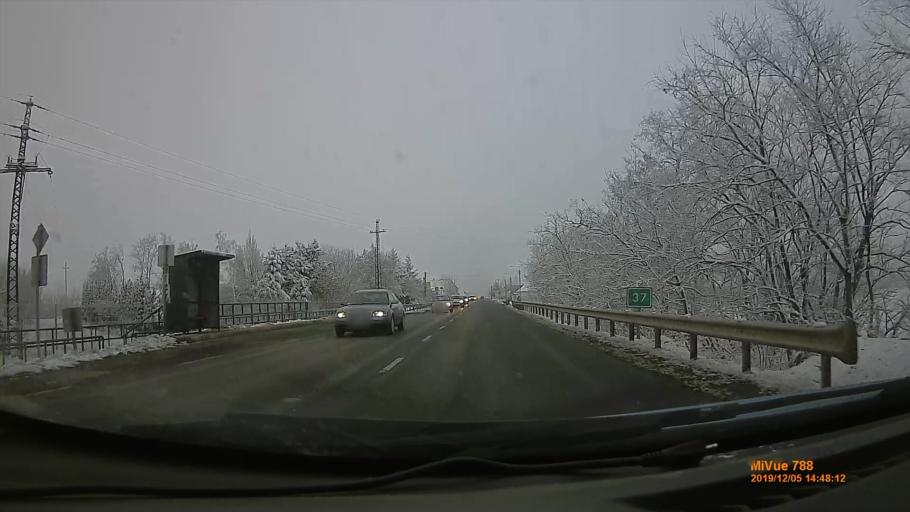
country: HU
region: Szabolcs-Szatmar-Bereg
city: Nyiregyhaza
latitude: 47.9746
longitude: 21.6899
